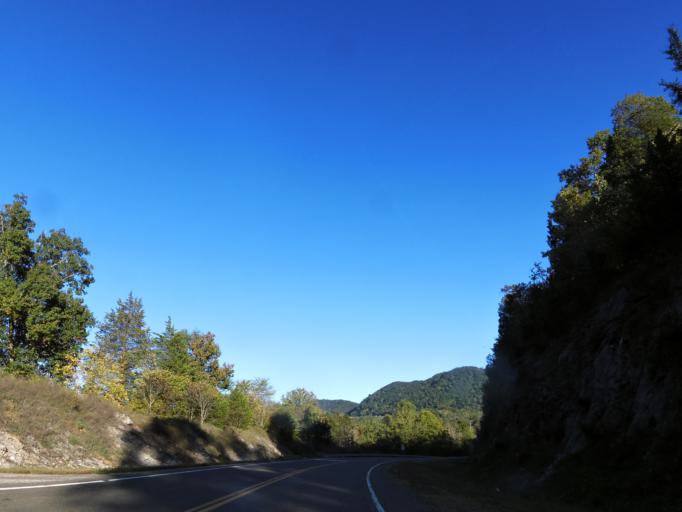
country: US
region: Tennessee
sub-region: Grainger County
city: Rutledge
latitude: 36.3554
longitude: -83.4323
